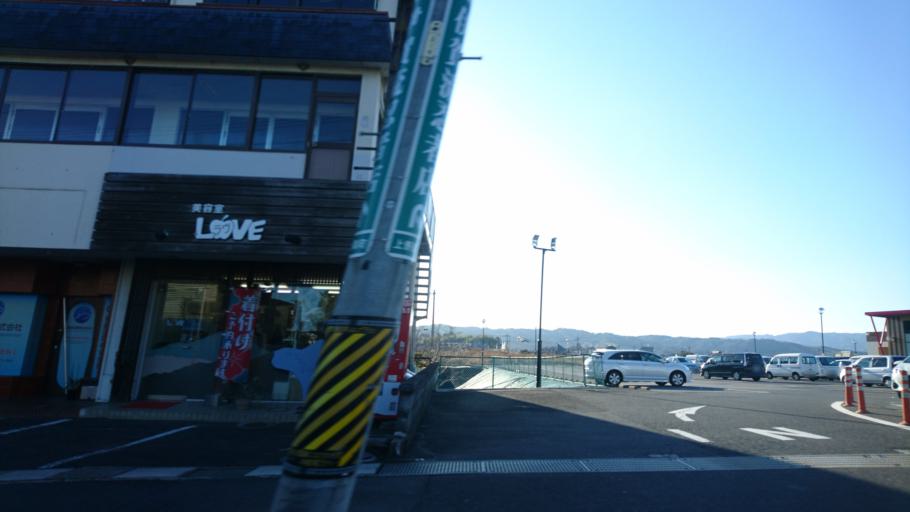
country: JP
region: Mie
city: Ueno-ebisumachi
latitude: 34.7553
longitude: 136.1327
